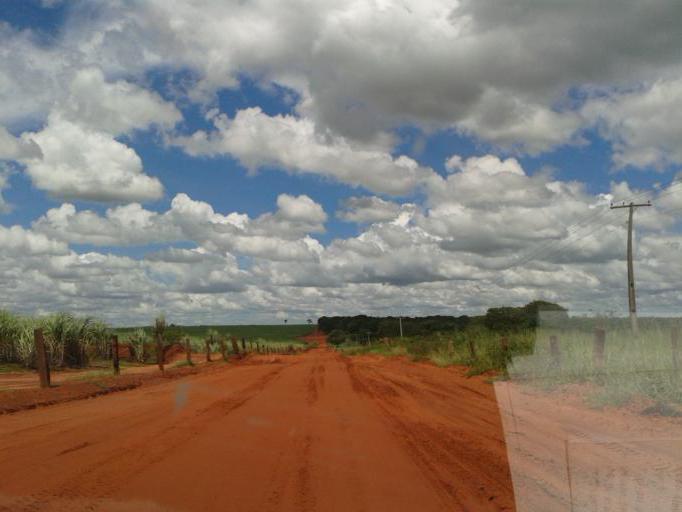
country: BR
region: Minas Gerais
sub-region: Santa Vitoria
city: Santa Vitoria
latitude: -18.8296
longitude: -50.0704
